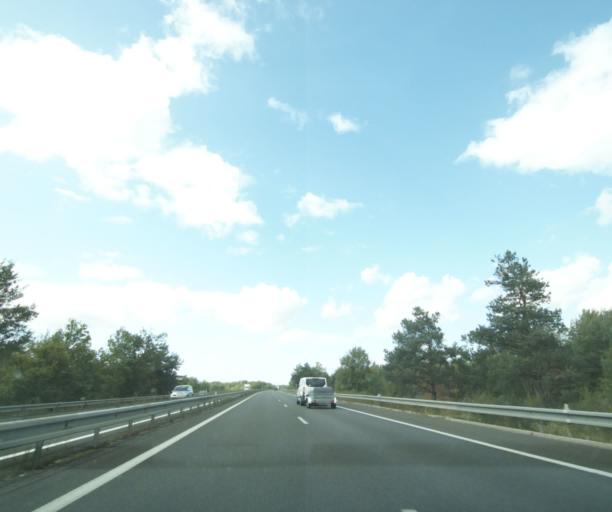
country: FR
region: Centre
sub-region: Departement du Loiret
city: Jouy-le-Potier
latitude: 47.7360
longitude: 1.8737
